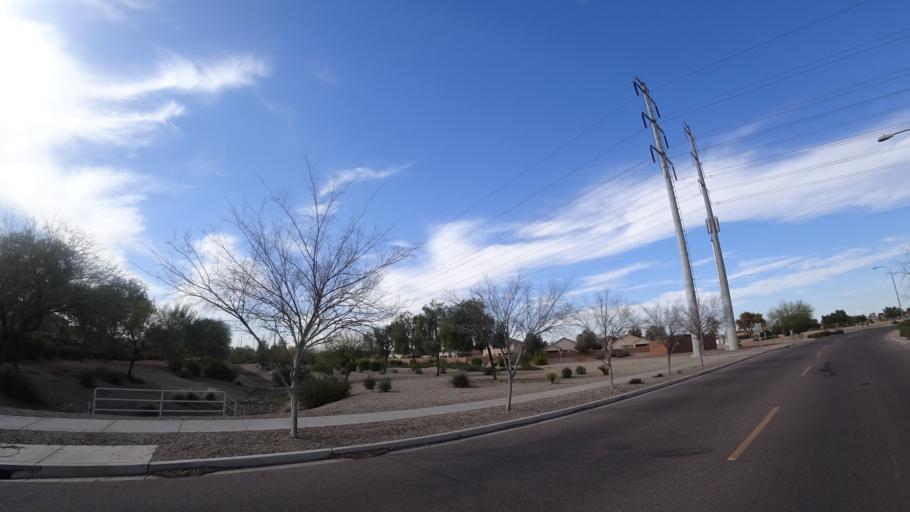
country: US
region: Arizona
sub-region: Maricopa County
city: Tolleson
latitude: 33.4132
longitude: -112.2808
